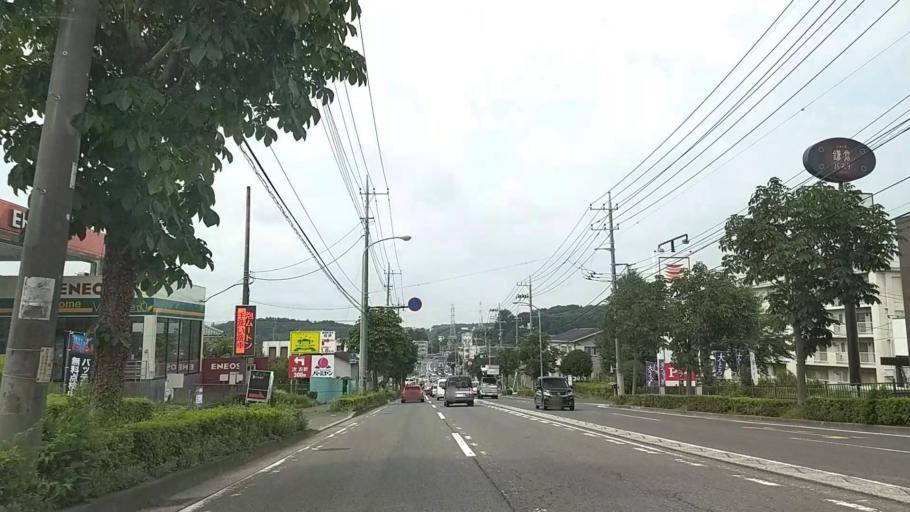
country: JP
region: Kanagawa
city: Minami-rinkan
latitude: 35.4877
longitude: 139.5238
